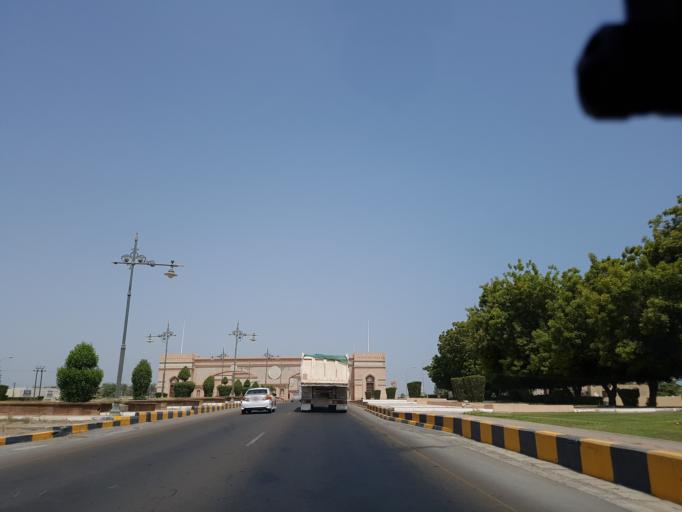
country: OM
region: Al Batinah
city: Saham
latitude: 24.2293
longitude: 56.8295
